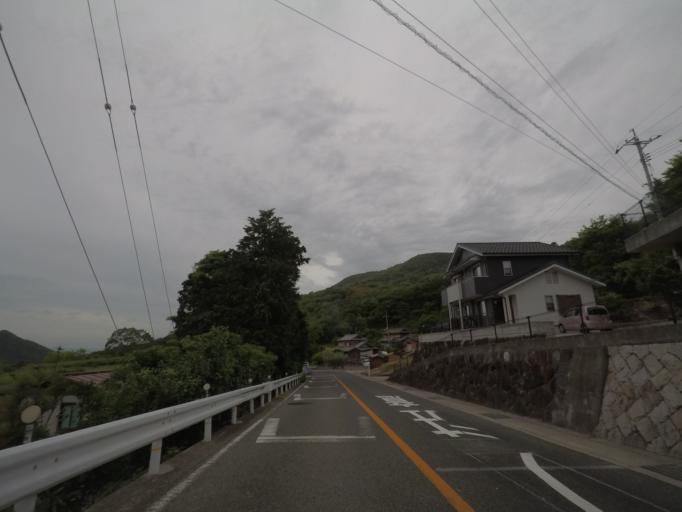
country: JP
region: Kagawa
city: Tonosho
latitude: 34.5020
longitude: 134.2140
